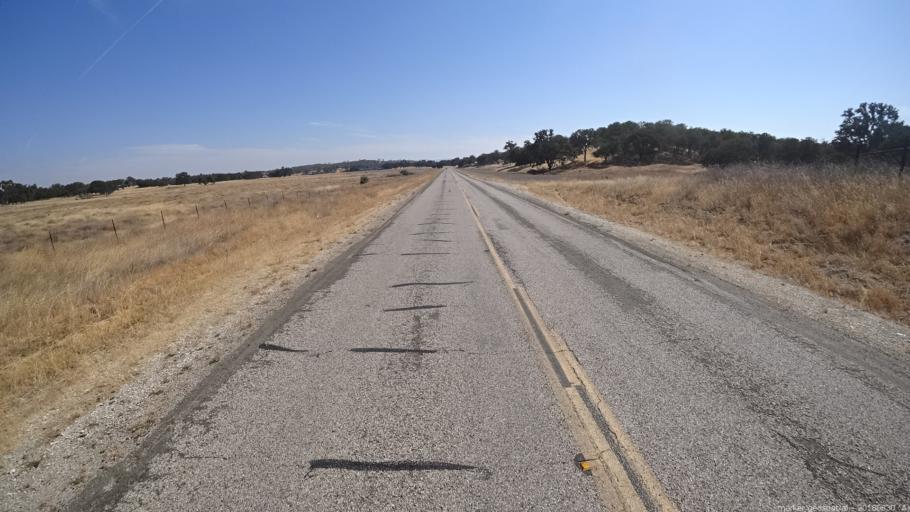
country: US
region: California
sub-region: Monterey County
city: King City
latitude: 36.0298
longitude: -121.1775
